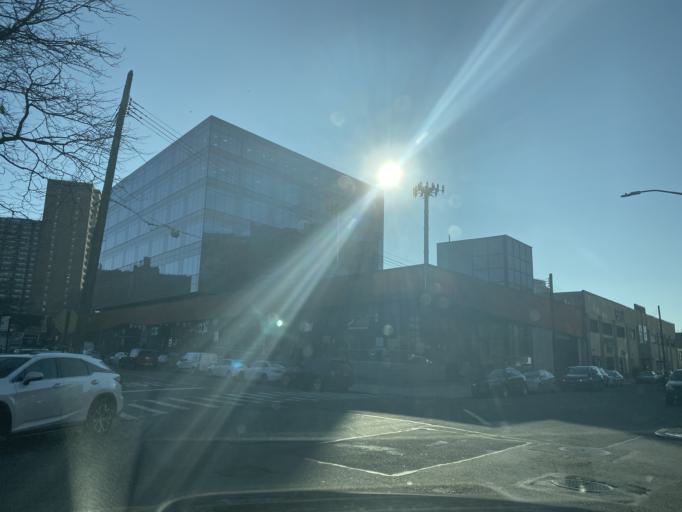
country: US
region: New York
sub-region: Kings County
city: Coney Island
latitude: 40.5793
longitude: -73.9762
